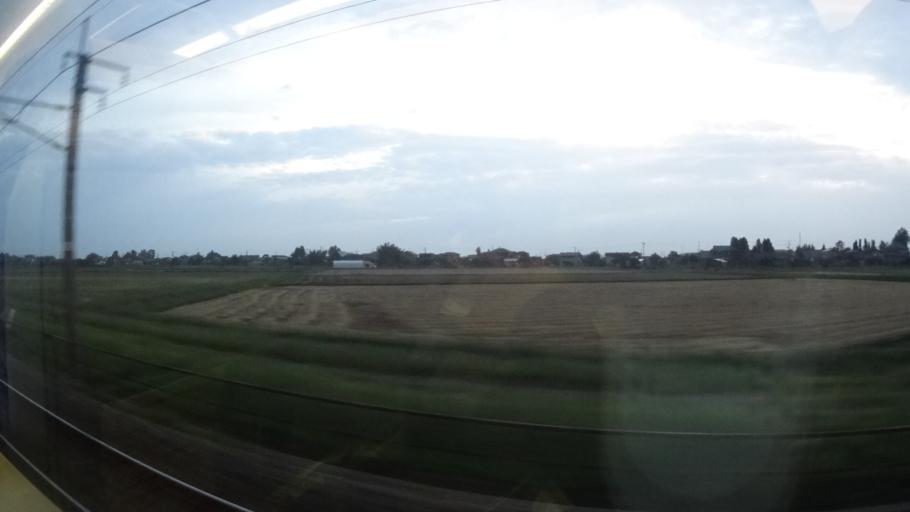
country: JP
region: Niigata
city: Shibata
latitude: 37.9880
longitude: 139.3640
